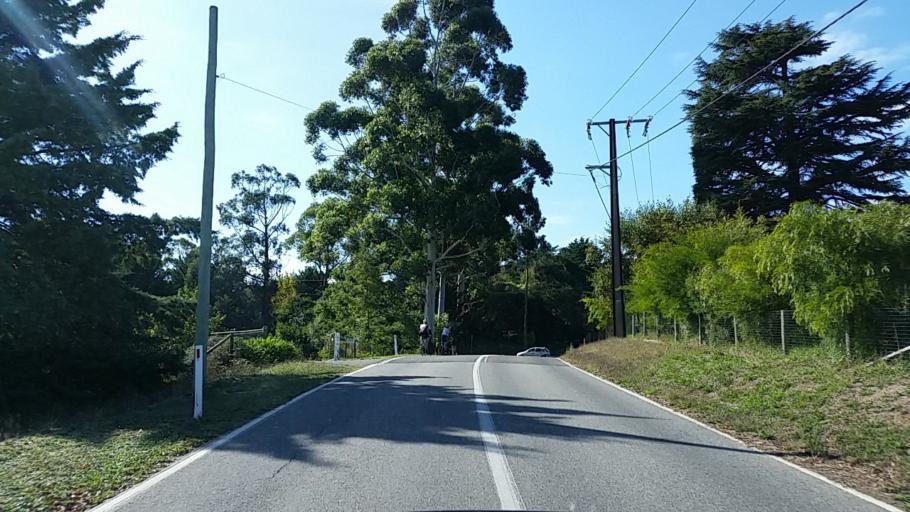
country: AU
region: South Australia
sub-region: Adelaide Hills
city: Adelaide Hills
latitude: -34.9433
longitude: 138.7285
